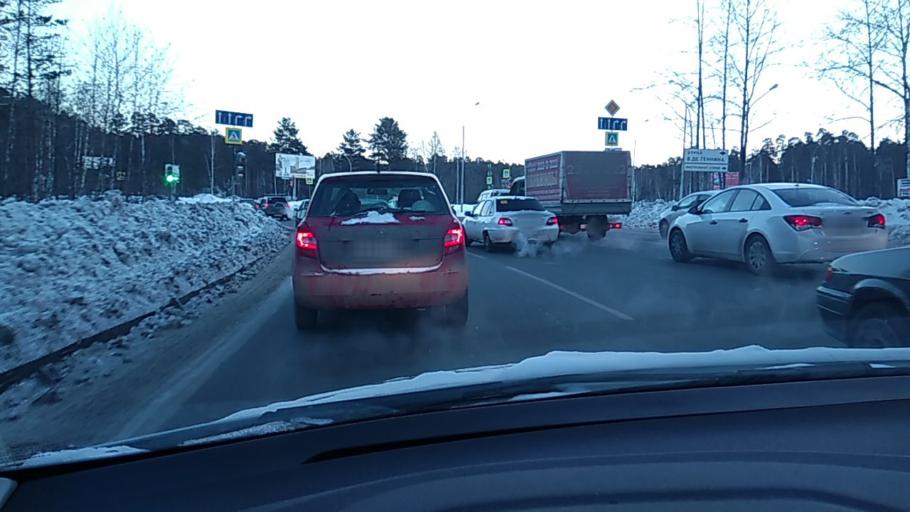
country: RU
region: Sverdlovsk
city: Sovkhoznyy
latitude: 56.8038
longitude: 60.5374
